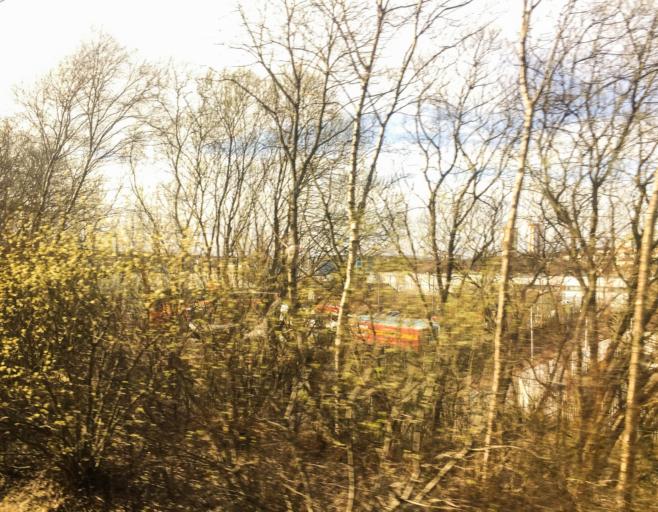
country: GB
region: Scotland
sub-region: East Dunbartonshire
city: Bishopbriggs
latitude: 55.8758
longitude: -4.2140
